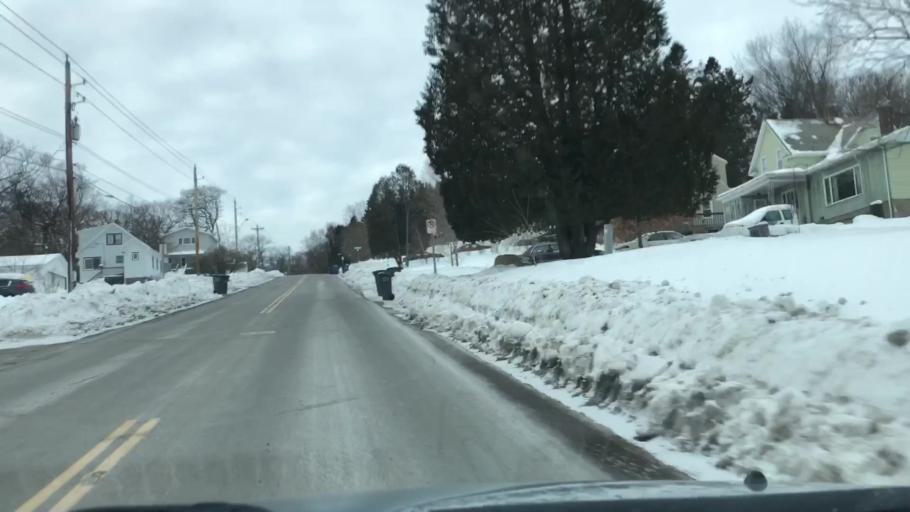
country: US
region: Minnesota
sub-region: Saint Louis County
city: Arnold
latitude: 46.8367
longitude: -92.0612
